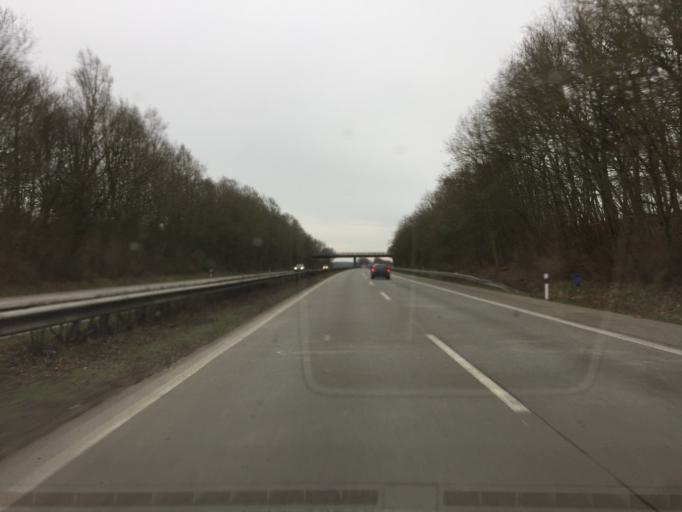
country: DE
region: Schleswig-Holstein
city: Ratekau
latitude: 53.9910
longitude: 10.7334
